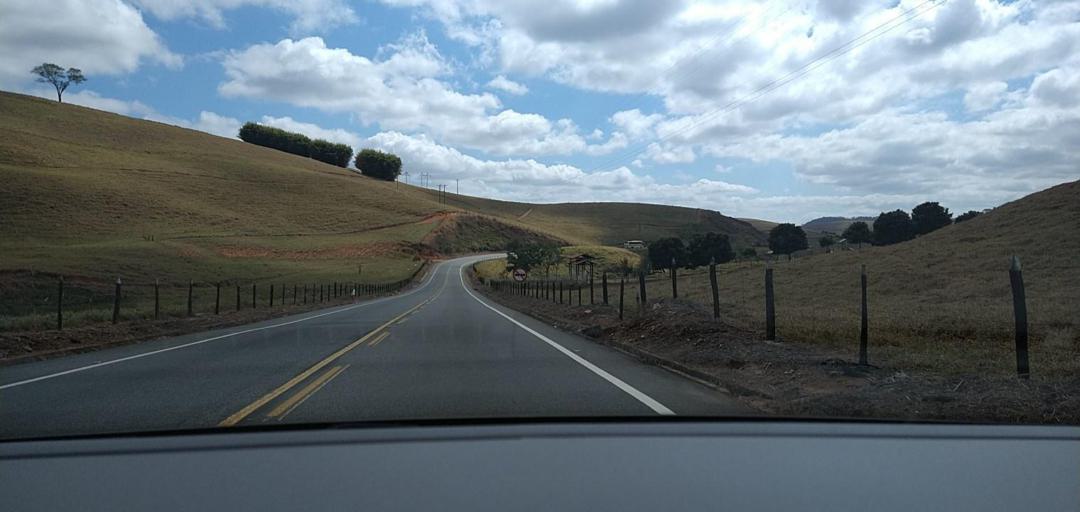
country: BR
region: Minas Gerais
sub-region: Ponte Nova
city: Ponte Nova
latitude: -20.4919
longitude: -42.8797
